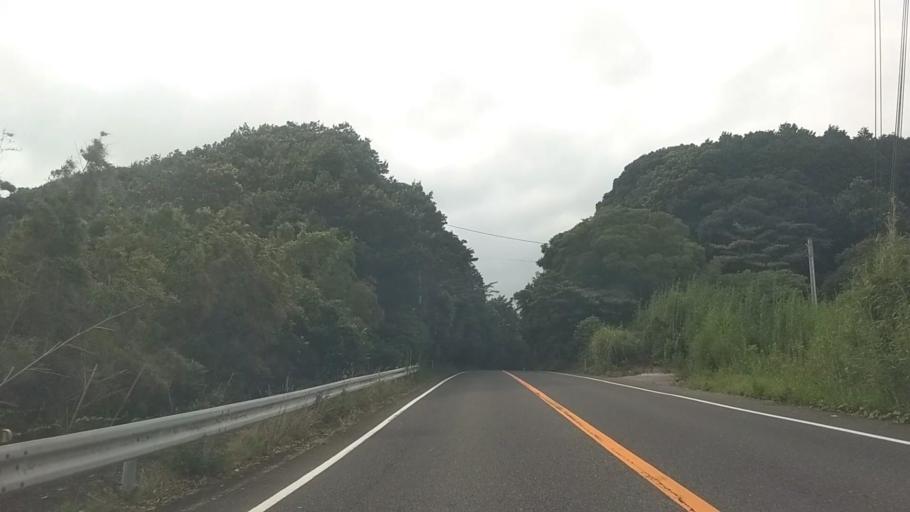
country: JP
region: Chiba
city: Kimitsu
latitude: 35.2343
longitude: 140.0101
